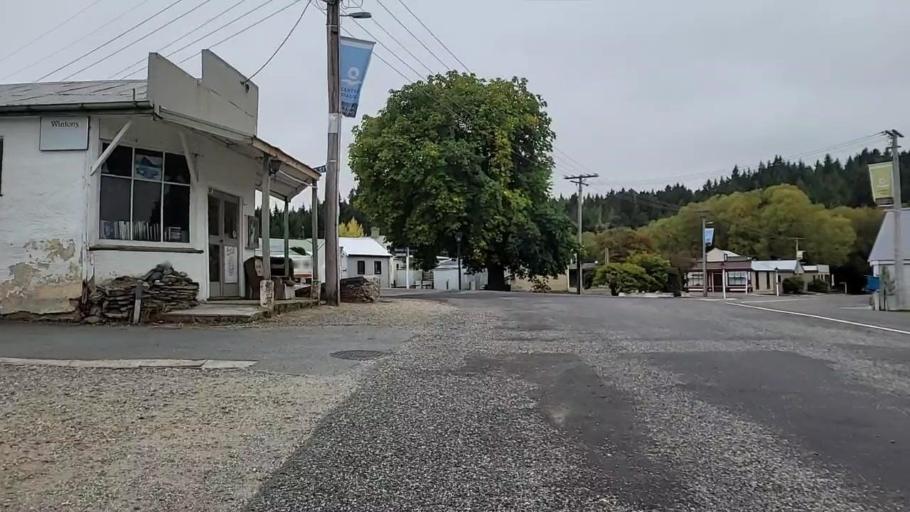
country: NZ
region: Otago
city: Oamaru
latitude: -45.0241
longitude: 170.1463
